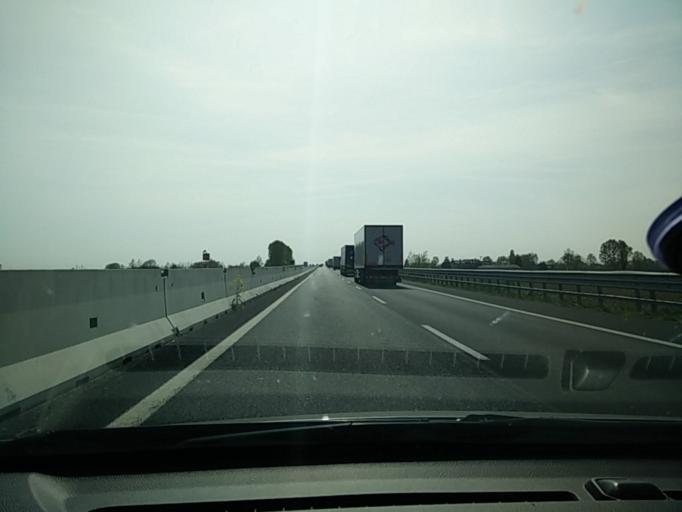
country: IT
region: Veneto
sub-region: Provincia di Venezia
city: Summaga
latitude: 45.7771
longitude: 12.7705
